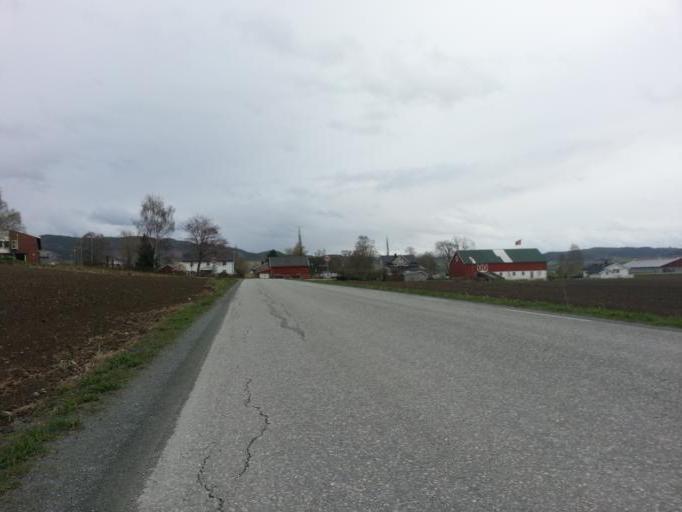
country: NO
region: Nord-Trondelag
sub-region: Levanger
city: Skogn
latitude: 63.6970
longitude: 11.1980
